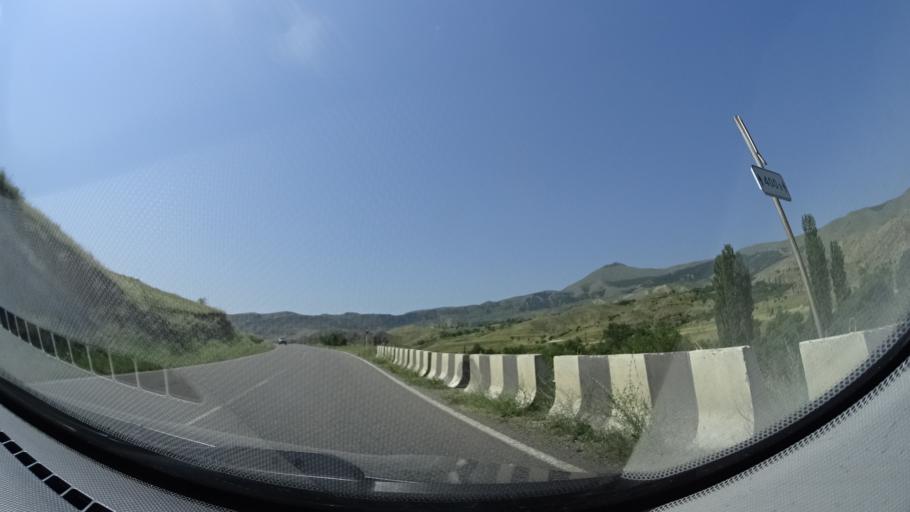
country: GE
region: Samtskhe-Javakheti
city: Aspindza
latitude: 41.5190
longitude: 43.2595
